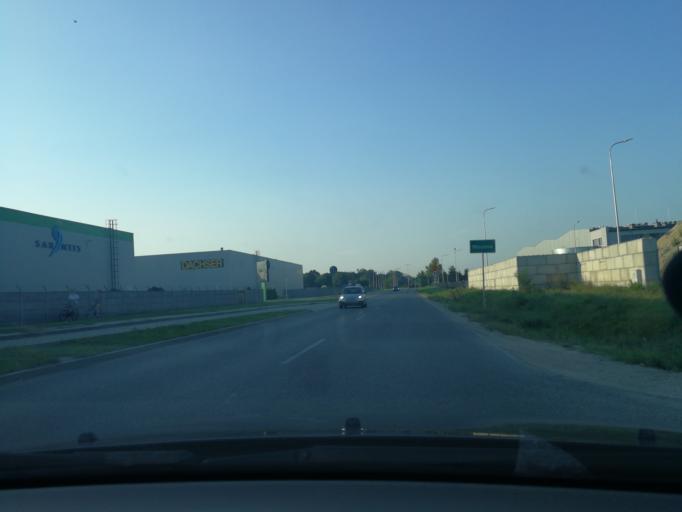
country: PL
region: Masovian Voivodeship
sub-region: Powiat pruszkowski
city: Brwinow
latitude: 52.1766
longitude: 20.7503
